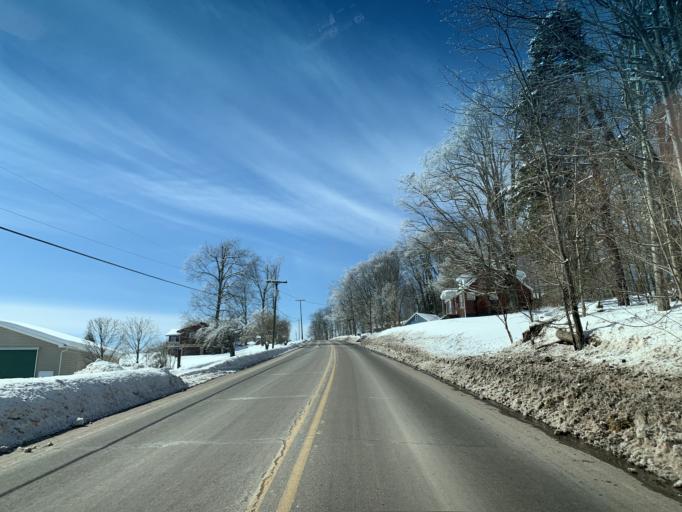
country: US
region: Pennsylvania
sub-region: Somerset County
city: Meyersdale
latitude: 39.7305
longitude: -79.1538
